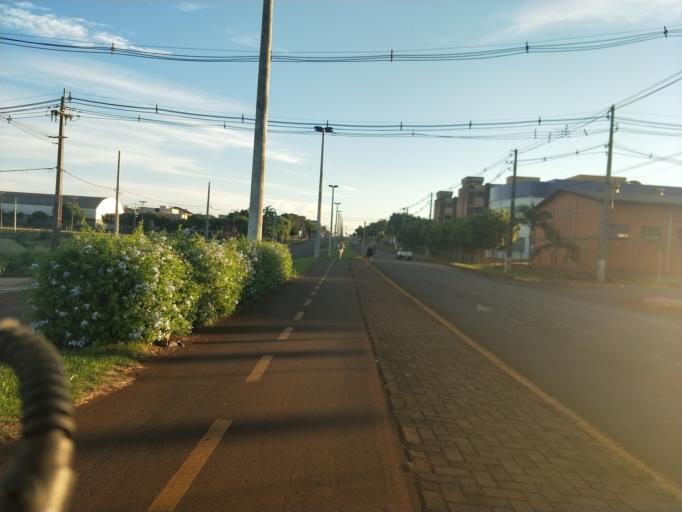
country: BR
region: Parana
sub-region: Marechal Candido Rondon
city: Marechal Candido Rondon
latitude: -24.5558
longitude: -54.0476
